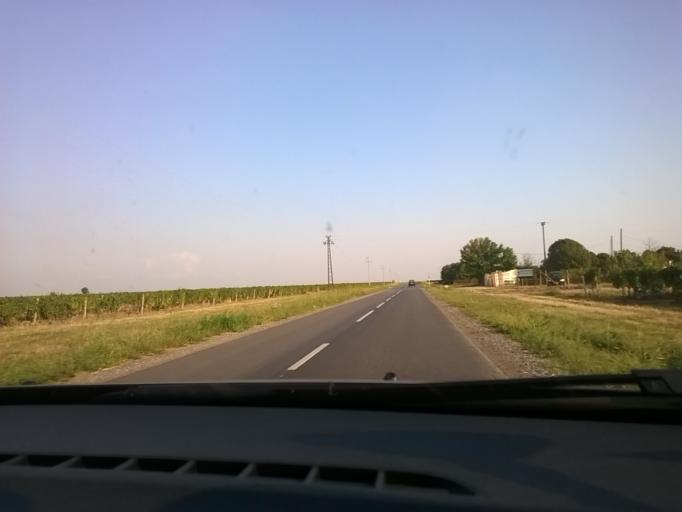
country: RS
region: Autonomna Pokrajina Vojvodina
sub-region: Juznobanatski Okrug
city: Vrsac
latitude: 45.1059
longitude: 21.3170
